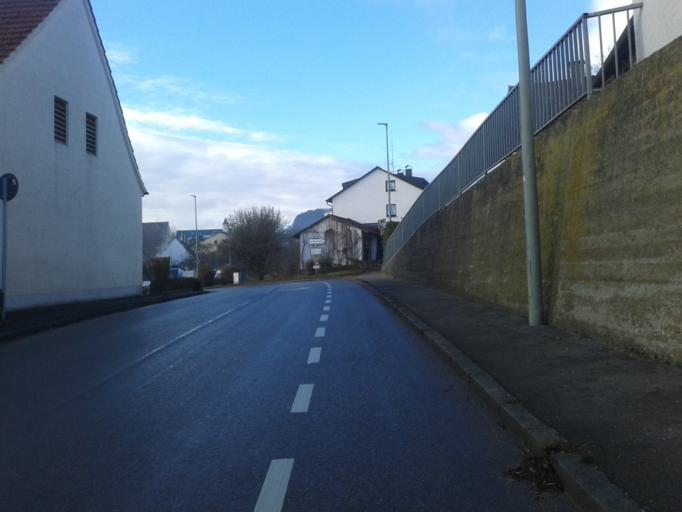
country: DE
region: Baden-Wuerttemberg
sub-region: Tuebingen Region
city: Erbach
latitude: 48.3825
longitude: 9.9005
